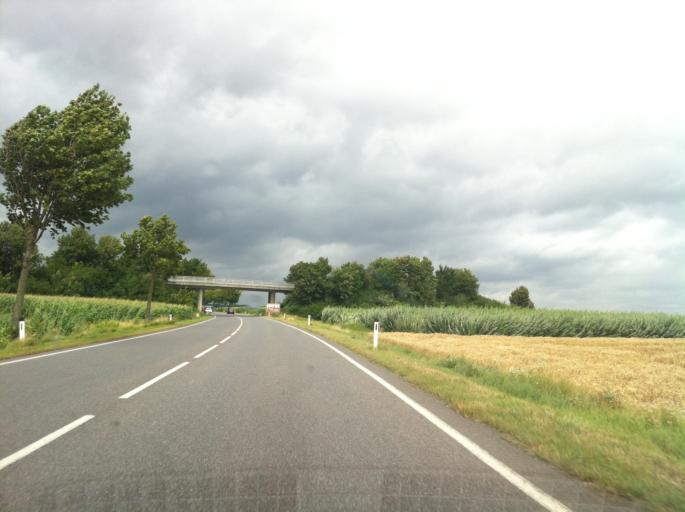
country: AT
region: Lower Austria
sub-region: Politischer Bezirk Tulln
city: Langenrohr
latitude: 48.3009
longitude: 16.0123
